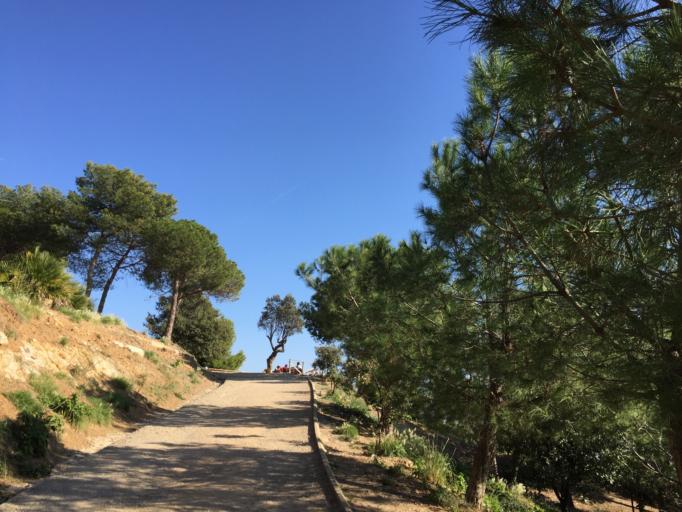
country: ES
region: Catalonia
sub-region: Provincia de Barcelona
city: Horta-Guinardo
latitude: 41.4183
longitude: 2.1661
